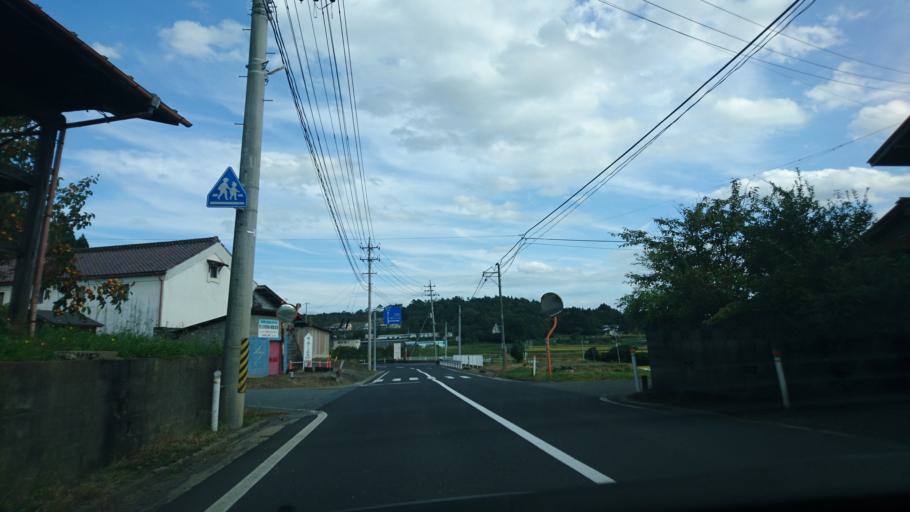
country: JP
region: Iwate
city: Ichinoseki
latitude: 38.8310
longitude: 141.2003
